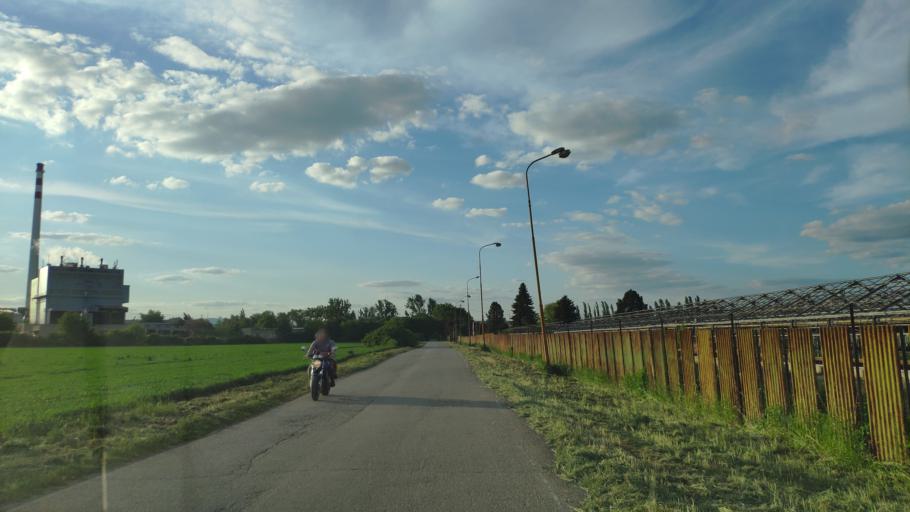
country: SK
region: Kosicky
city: Kosice
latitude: 48.6546
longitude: 21.3167
